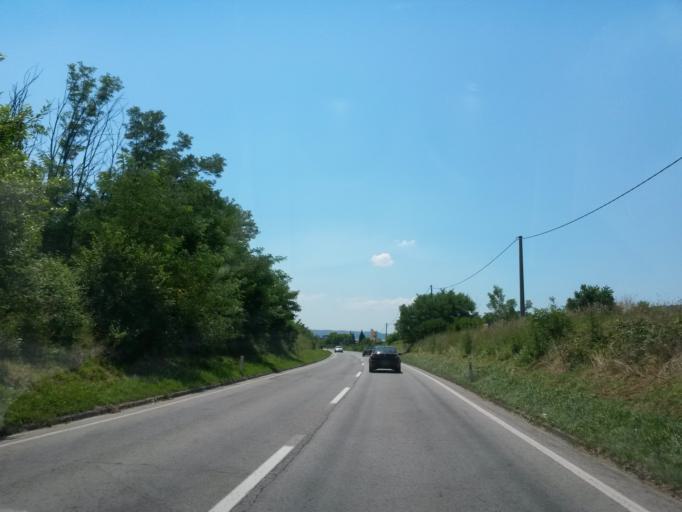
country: BA
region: Republika Srpska
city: Doboj
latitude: 44.8157
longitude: 18.0523
